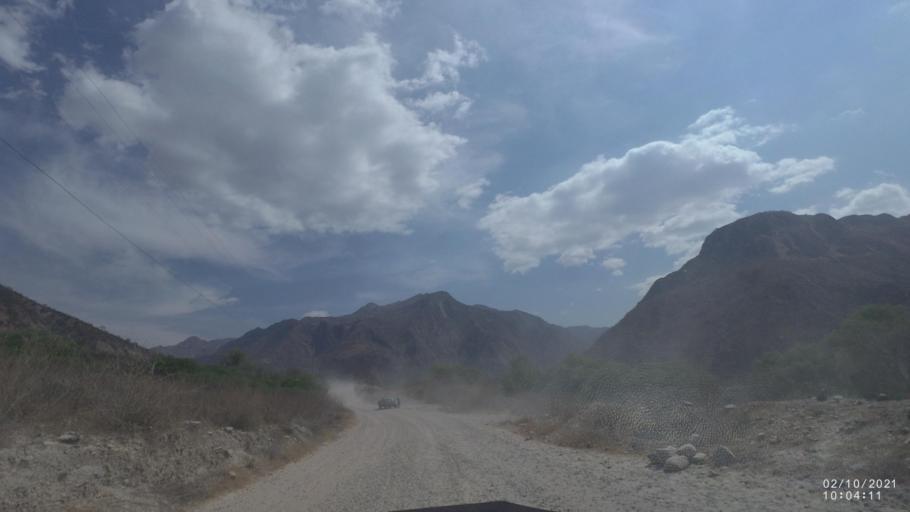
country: BO
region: Cochabamba
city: Irpa Irpa
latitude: -17.7525
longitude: -66.3525
